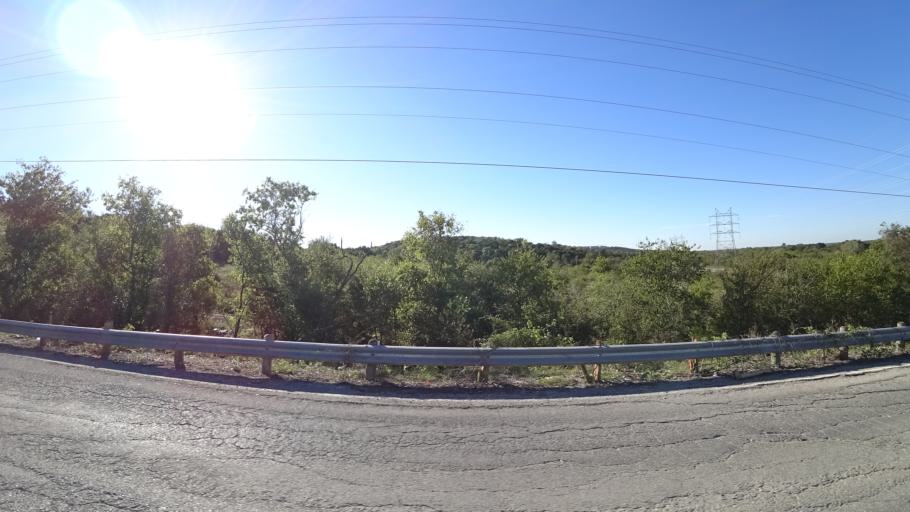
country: US
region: Texas
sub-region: Travis County
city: Manor
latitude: 30.3245
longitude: -97.6434
